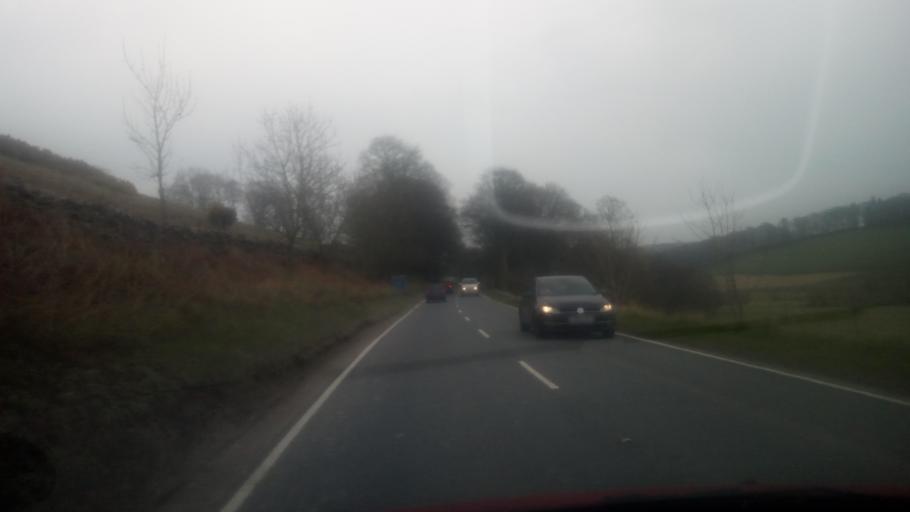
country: GB
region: Scotland
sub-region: The Scottish Borders
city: Galashiels
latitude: 55.7001
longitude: -2.8789
